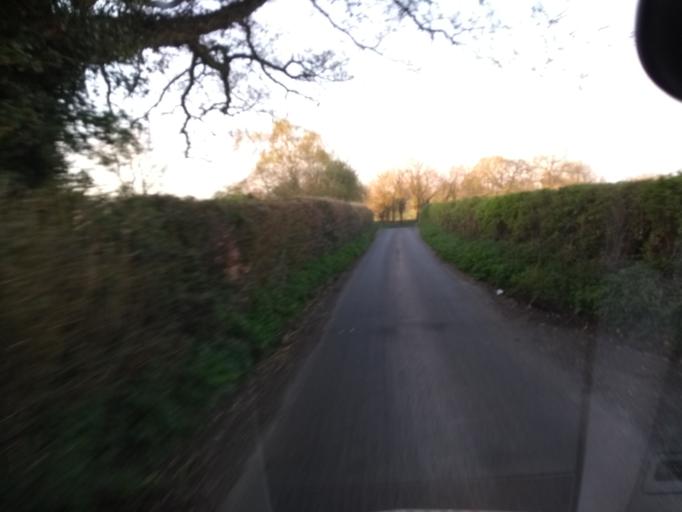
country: GB
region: England
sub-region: Somerset
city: Chard
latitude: 50.8623
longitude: -2.9181
